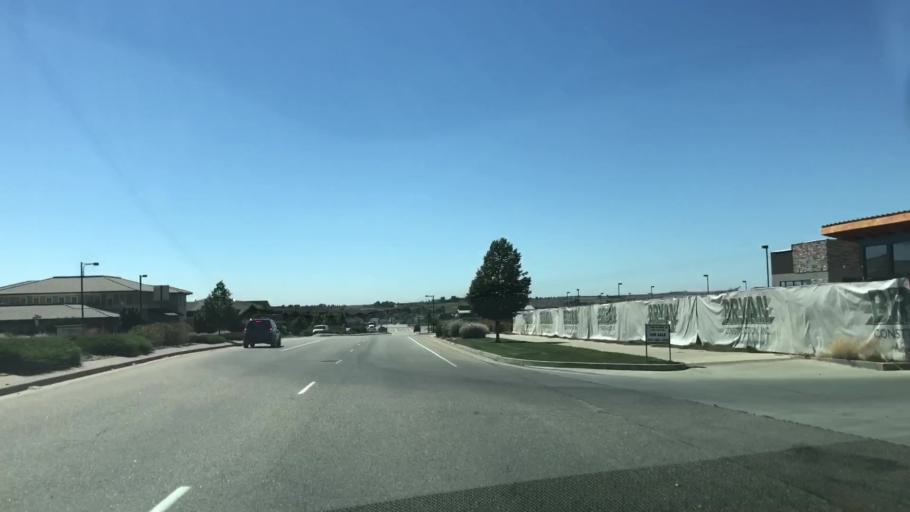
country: US
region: Colorado
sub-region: Weld County
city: Johnstown
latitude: 40.4062
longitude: -104.9739
